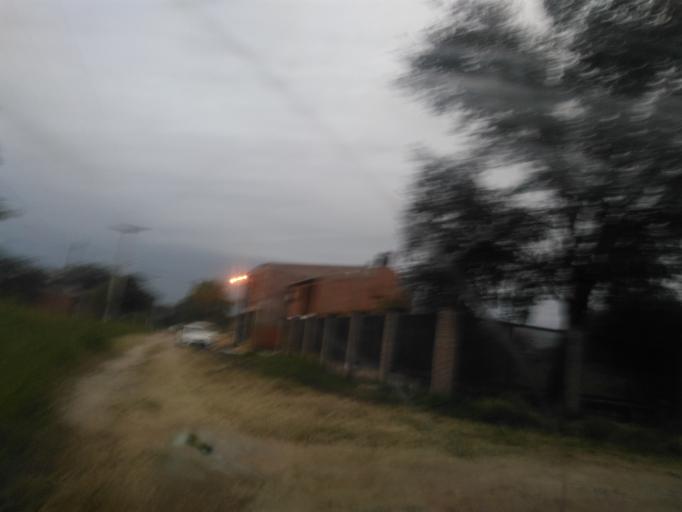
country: AR
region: Chaco
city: Fontana
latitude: -27.4418
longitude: -59.0246
